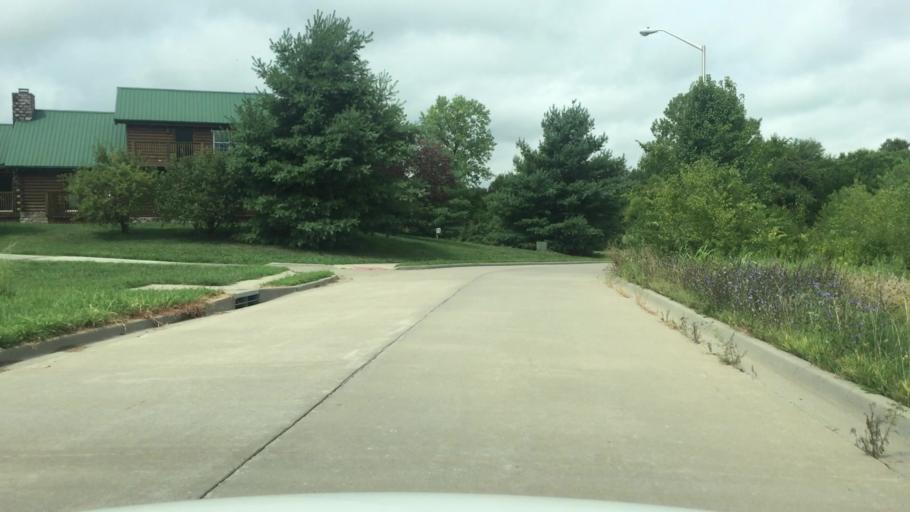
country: US
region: Missouri
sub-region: Jackson County
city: Lone Jack
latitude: 38.8804
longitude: -94.2125
